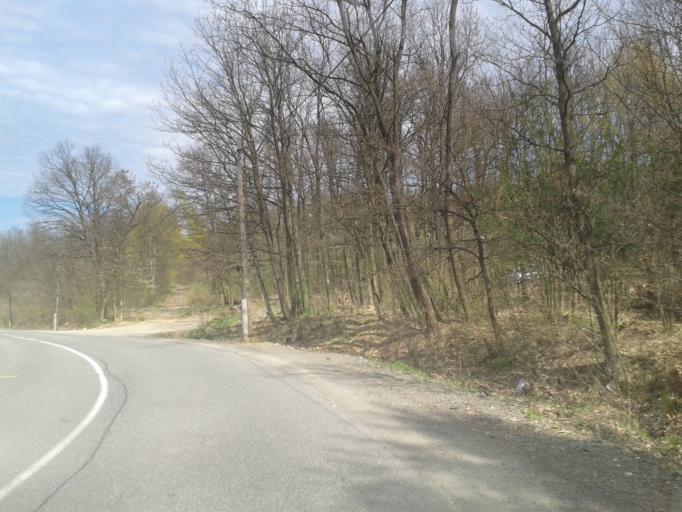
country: CZ
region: Central Bohemia
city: Vrane nad Vltavou
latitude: 49.9490
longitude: 14.3773
